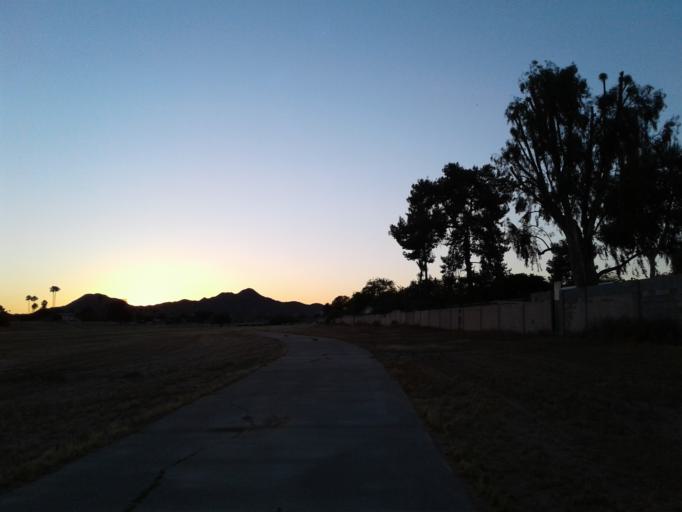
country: US
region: Arizona
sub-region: Maricopa County
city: Paradise Valley
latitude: 33.6013
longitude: -111.9994
